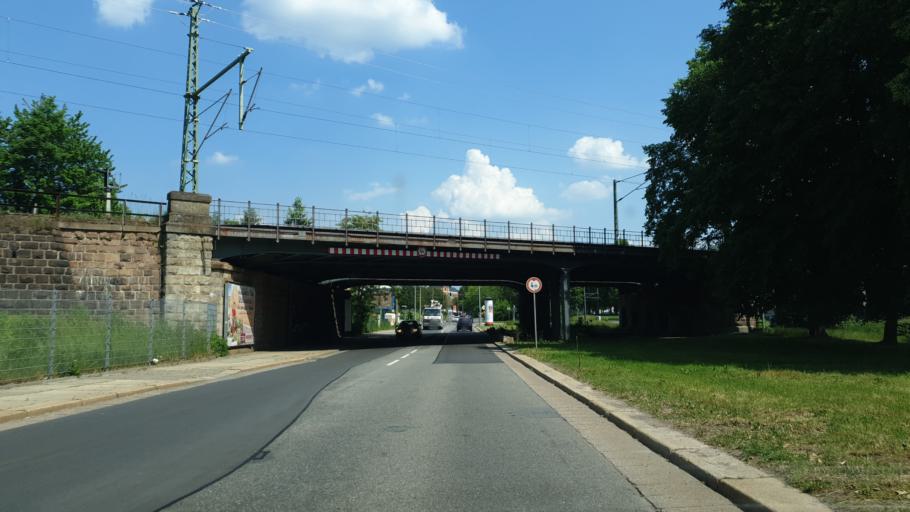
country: DE
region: Saxony
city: Chemnitz
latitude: 50.8317
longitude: 12.9335
